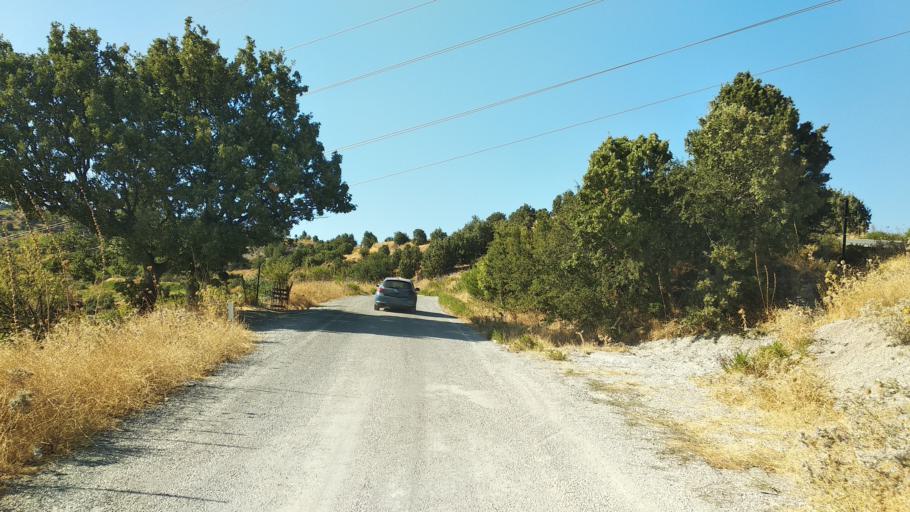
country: TR
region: Izmir
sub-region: Seferihisar
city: Seferhisar
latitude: 38.3270
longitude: 26.9509
